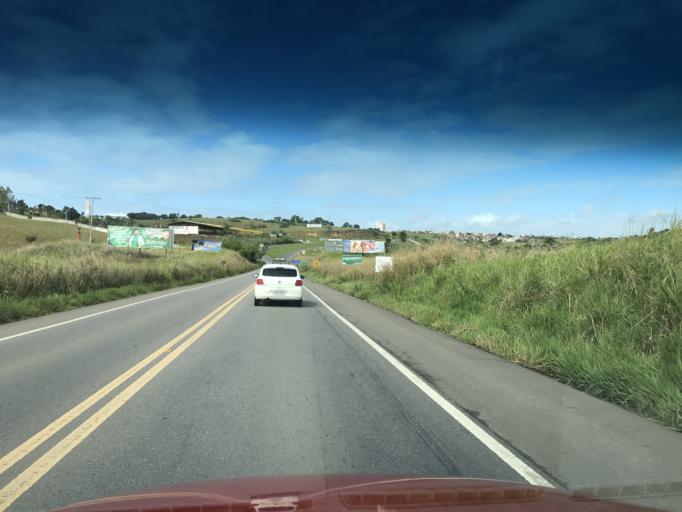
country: BR
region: Bahia
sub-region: Santo Antonio De Jesus
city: Santo Antonio de Jesus
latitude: -12.9455
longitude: -39.2521
